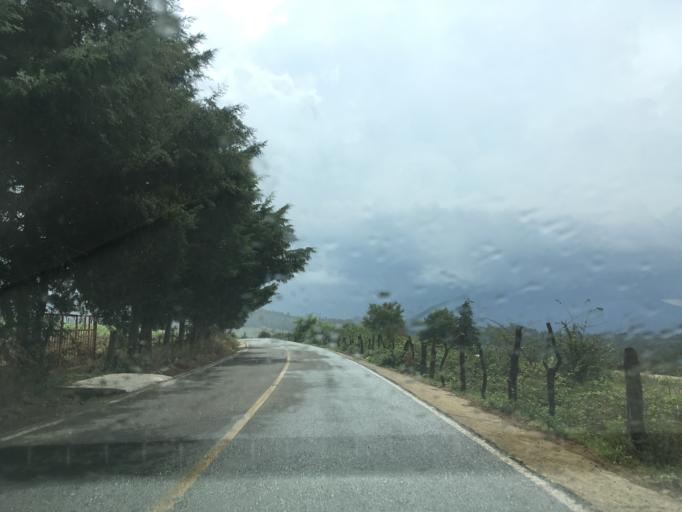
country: MX
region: Michoacan
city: Acuitzio del Canje
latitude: 19.5287
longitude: -101.2400
